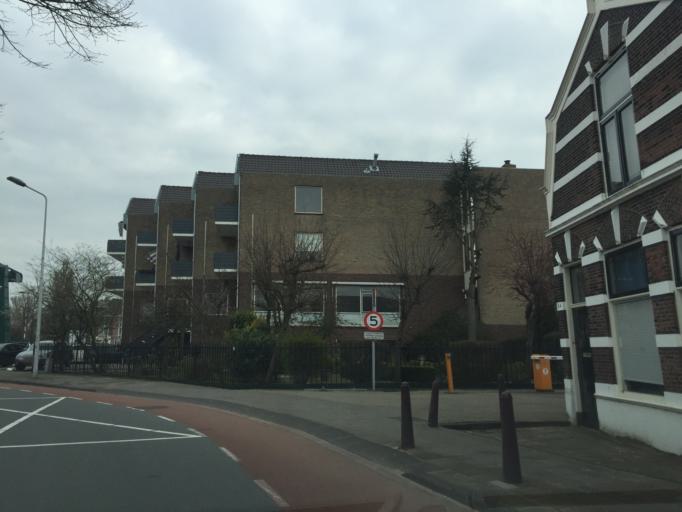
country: NL
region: South Holland
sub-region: Gemeente Leiden
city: Leiden
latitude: 52.1607
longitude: 4.5062
